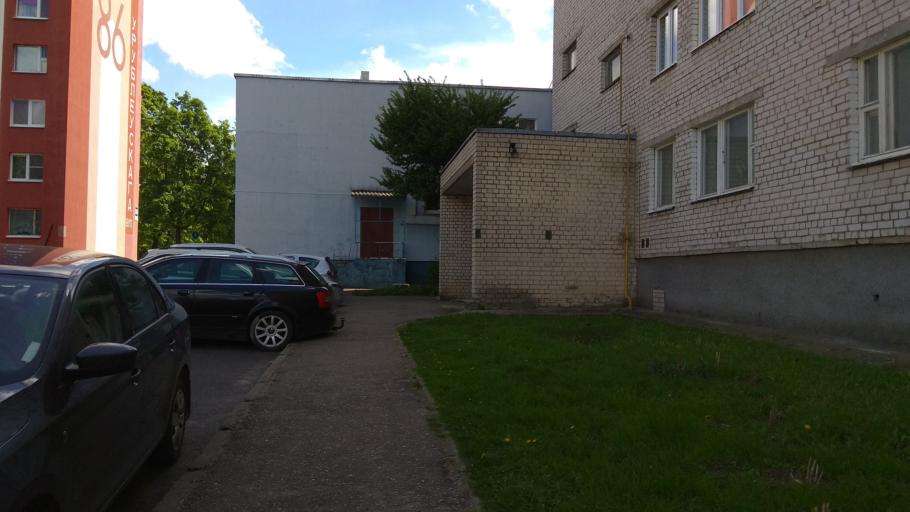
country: BY
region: Grodnenskaya
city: Hrodna
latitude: 53.7072
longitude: 23.8036
